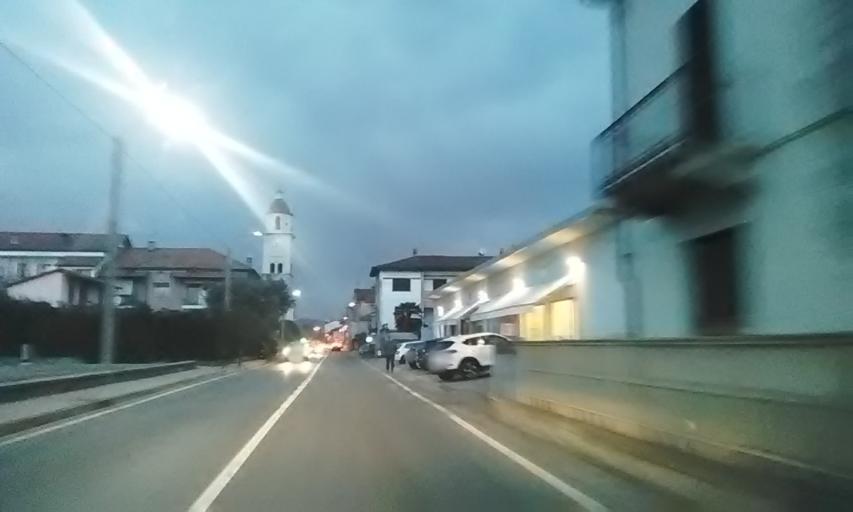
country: IT
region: Piedmont
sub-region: Provincia di Torino
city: Montalto Dora
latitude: 45.4898
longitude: 7.8620
